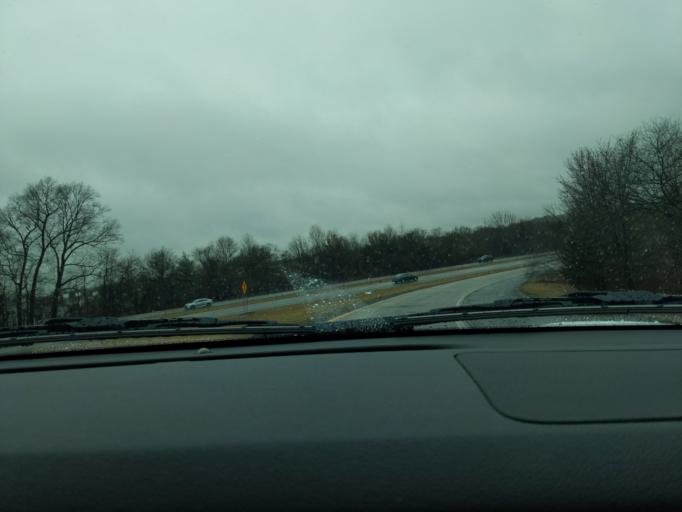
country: US
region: Pennsylvania
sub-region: Bucks County
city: Doylestown
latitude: 40.3050
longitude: -75.1486
